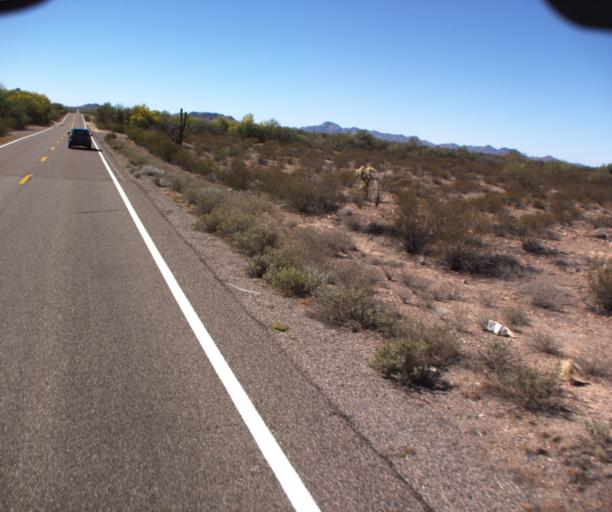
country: US
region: Arizona
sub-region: Pima County
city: Ajo
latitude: 32.1515
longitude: -112.7652
